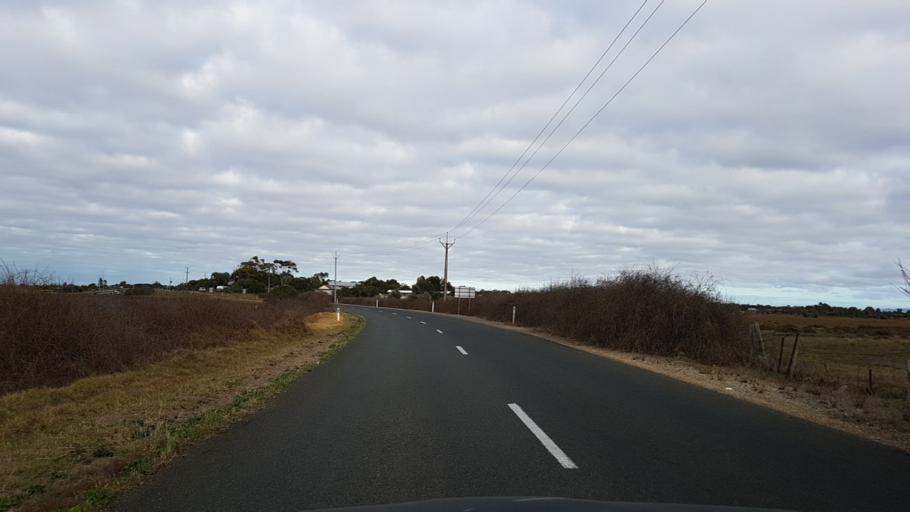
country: AU
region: South Australia
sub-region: Alexandrina
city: Langhorne Creek
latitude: -35.4000
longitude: 138.9845
